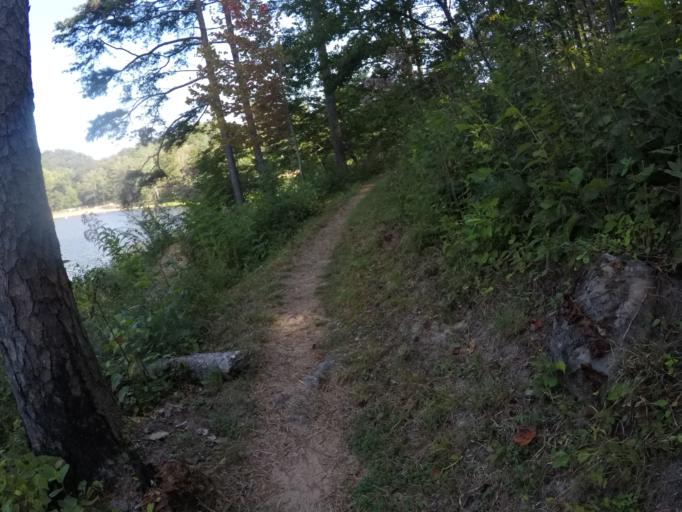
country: US
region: Ohio
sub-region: Lawrence County
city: Ironton
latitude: 38.6181
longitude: -82.6271
